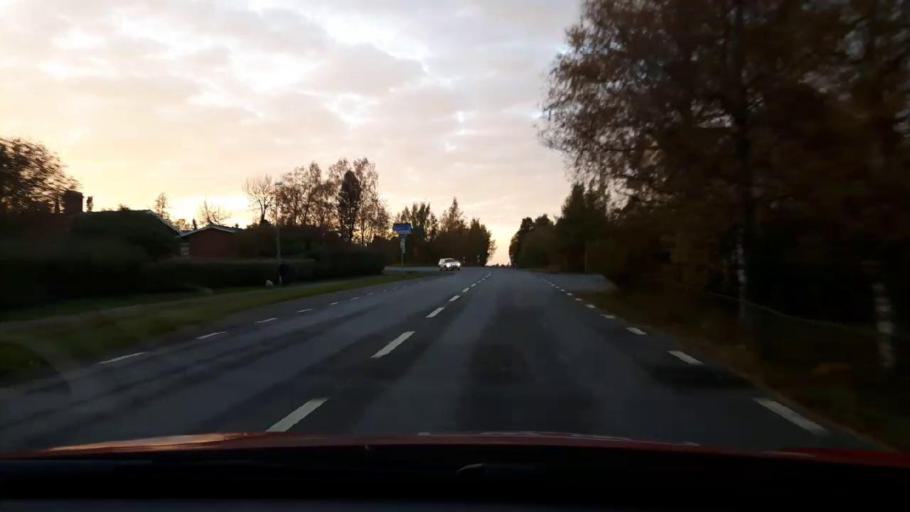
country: SE
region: Jaemtland
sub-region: OEstersunds Kommun
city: Ostersund
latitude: 63.2469
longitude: 14.5707
